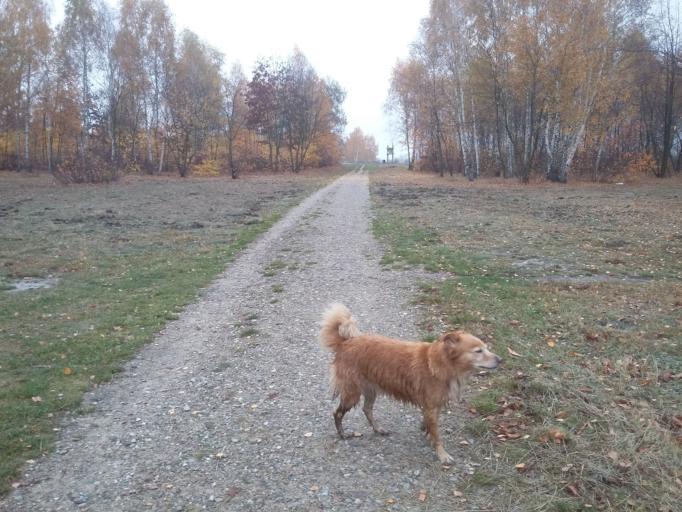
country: PL
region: Lodz Voivodeship
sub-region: Powiat pabianicki
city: Ksawerow
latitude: 51.7293
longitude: 19.3847
